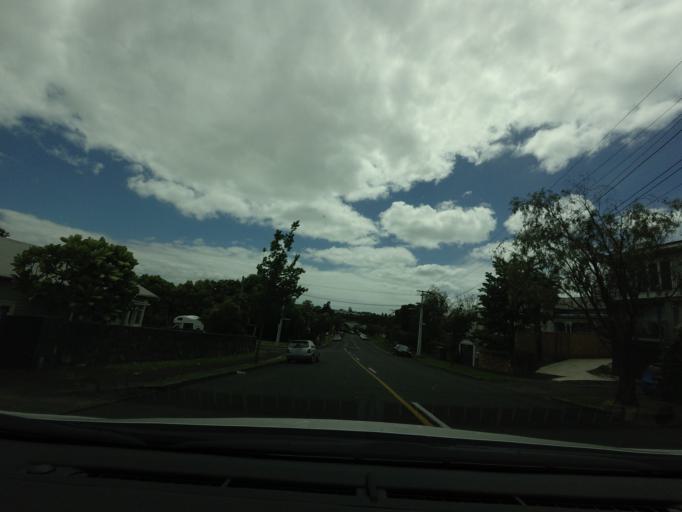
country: NZ
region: Auckland
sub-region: Auckland
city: Auckland
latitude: -36.8720
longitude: 174.7330
